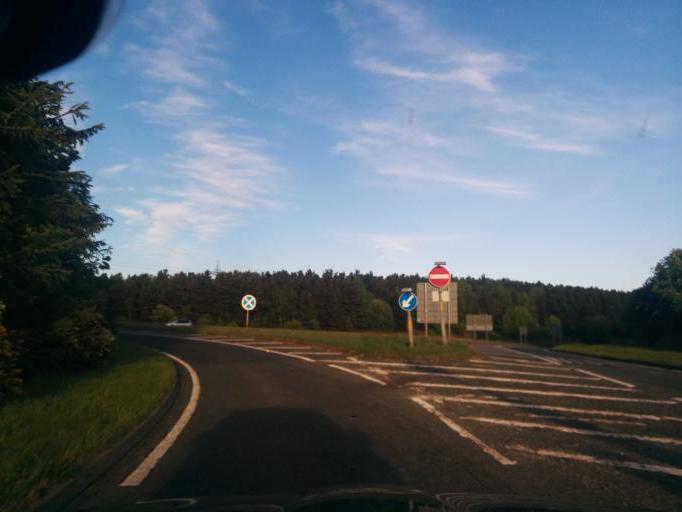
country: GB
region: England
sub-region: Northumberland
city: Cramlington
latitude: 55.0978
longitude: -1.5681
